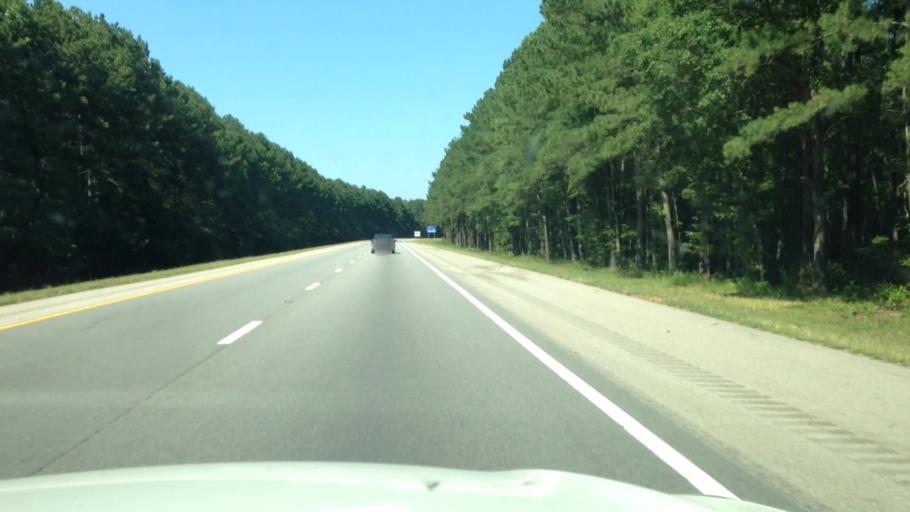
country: US
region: North Carolina
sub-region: Wilson County
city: Lucama
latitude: 35.7130
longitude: -78.0386
